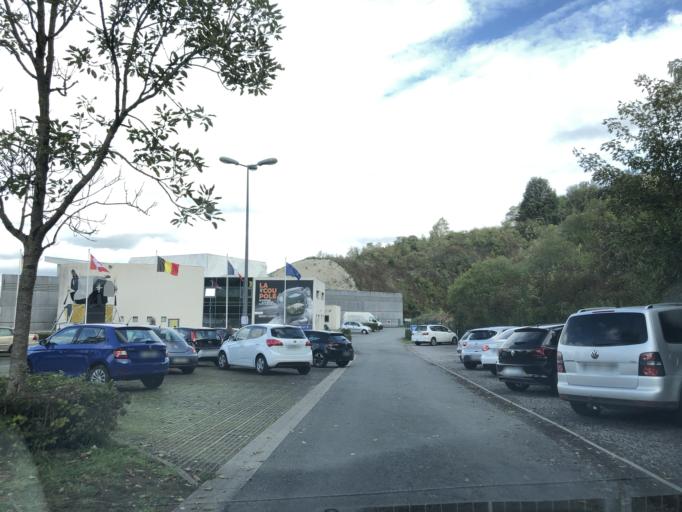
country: FR
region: Nord-Pas-de-Calais
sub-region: Departement du Pas-de-Calais
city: Wizernes
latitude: 50.7052
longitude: 2.2408
